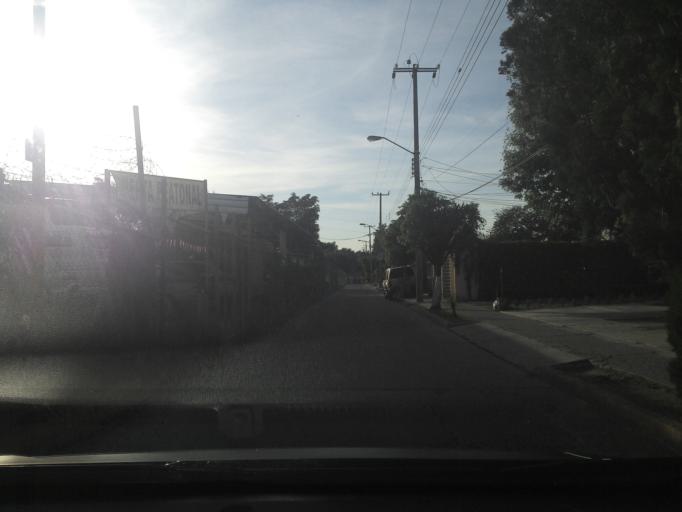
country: MX
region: Jalisco
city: Tlaquepaque
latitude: 20.6203
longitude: -103.3237
